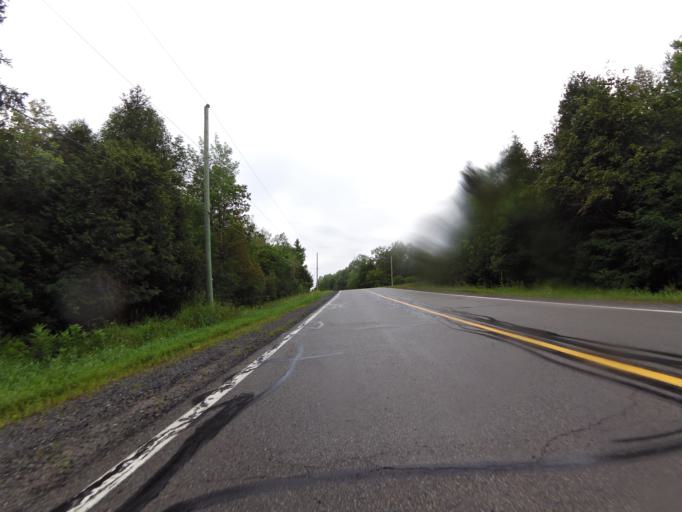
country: CA
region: Ontario
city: Perth
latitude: 45.0001
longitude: -76.3764
